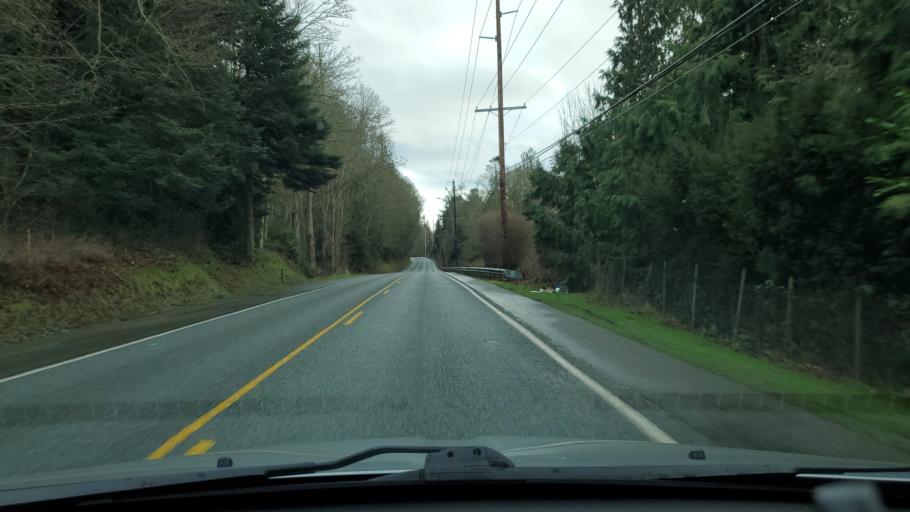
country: US
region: Washington
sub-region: Skagit County
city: Anacortes
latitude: 48.4533
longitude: -122.5460
